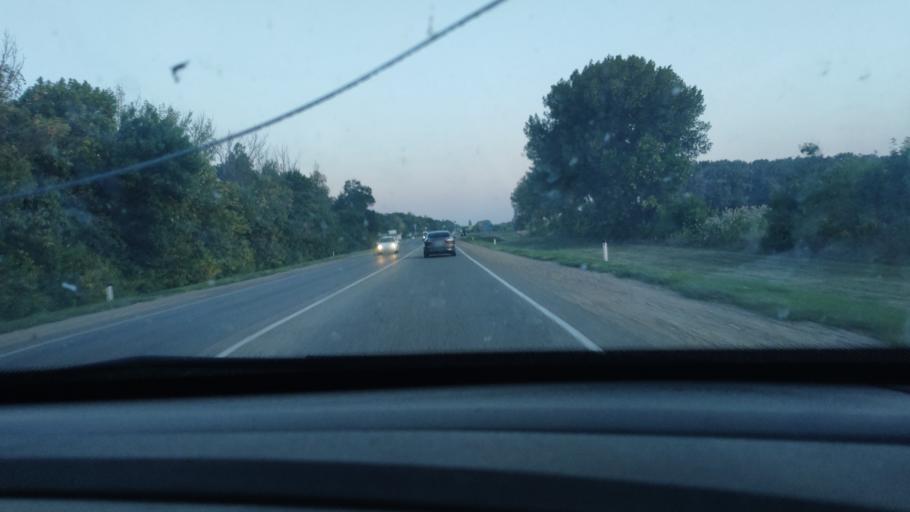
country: RU
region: Krasnodarskiy
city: Medvedovskaya
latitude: 45.4570
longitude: 38.9877
